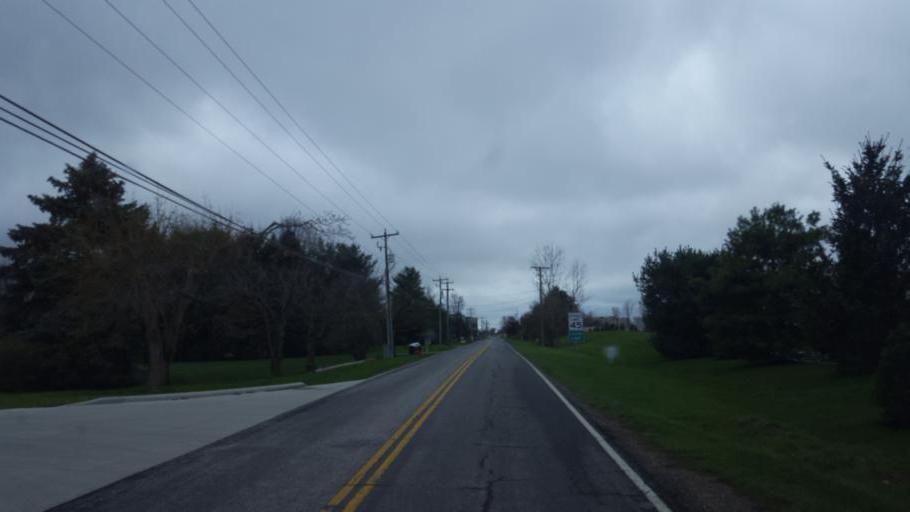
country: US
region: Ohio
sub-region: Franklin County
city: Westerville
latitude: 40.1442
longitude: -82.9602
